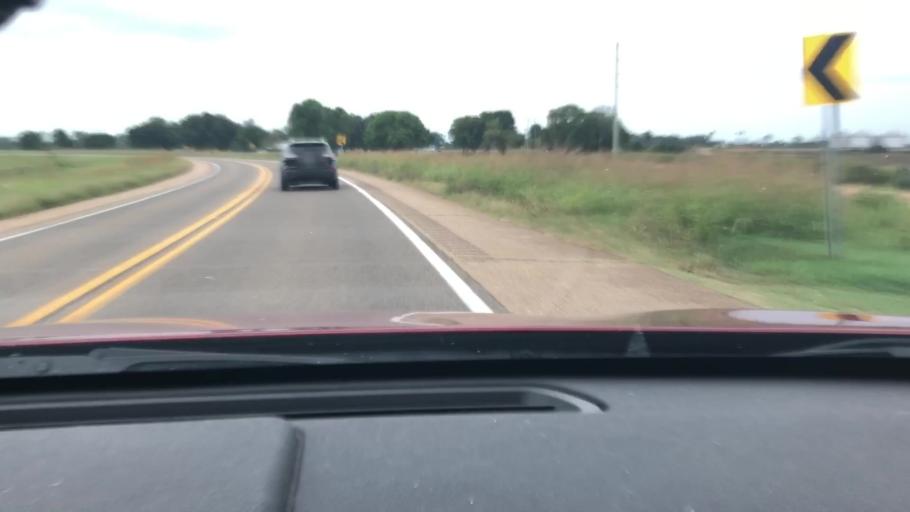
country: US
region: Arkansas
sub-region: Lafayette County
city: Lewisville
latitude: 33.3789
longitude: -93.7359
